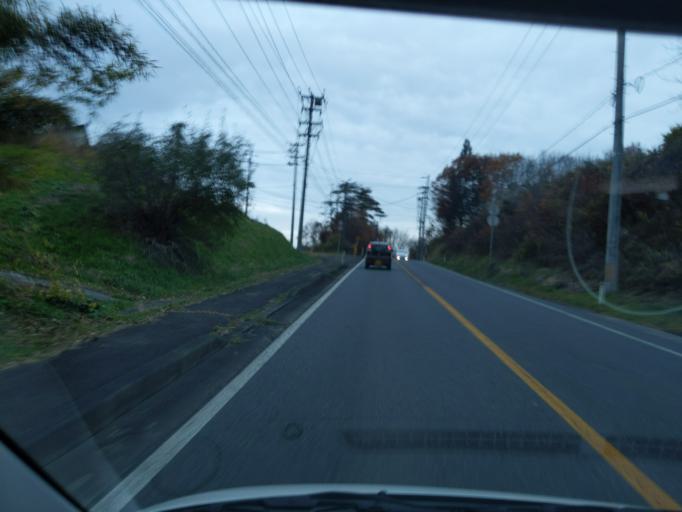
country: JP
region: Iwate
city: Ichinoseki
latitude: 39.0113
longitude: 141.3282
